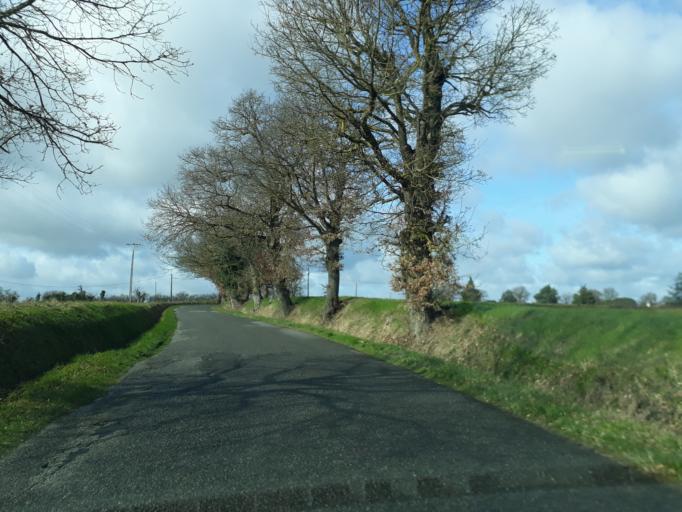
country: FR
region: Midi-Pyrenees
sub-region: Departement du Gers
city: Gimont
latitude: 43.6326
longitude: 1.0103
